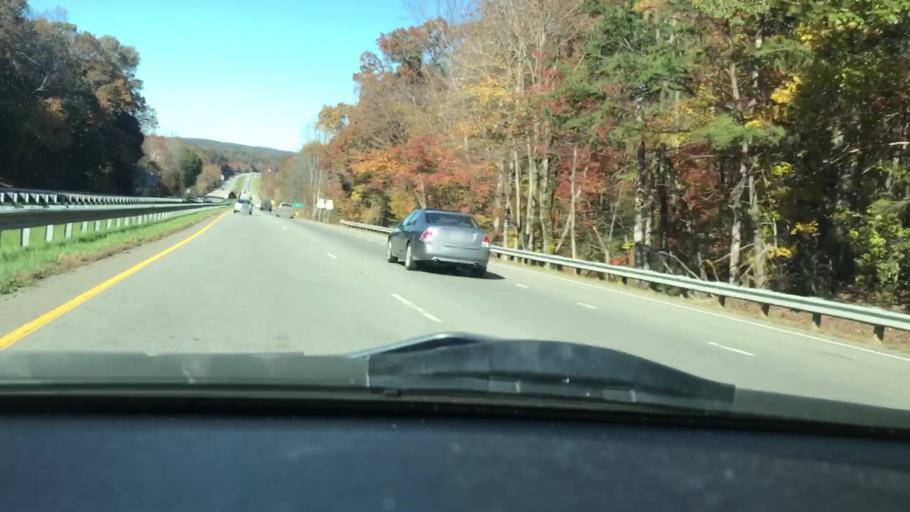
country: US
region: North Carolina
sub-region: Rockingham County
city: Madison
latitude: 36.3790
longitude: -79.9412
